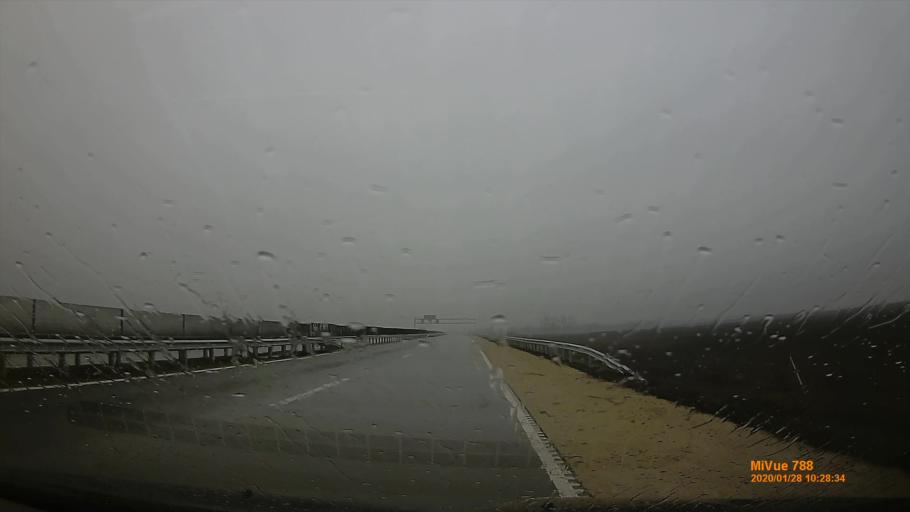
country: HU
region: Pest
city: Pilis
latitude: 47.3177
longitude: 19.5457
